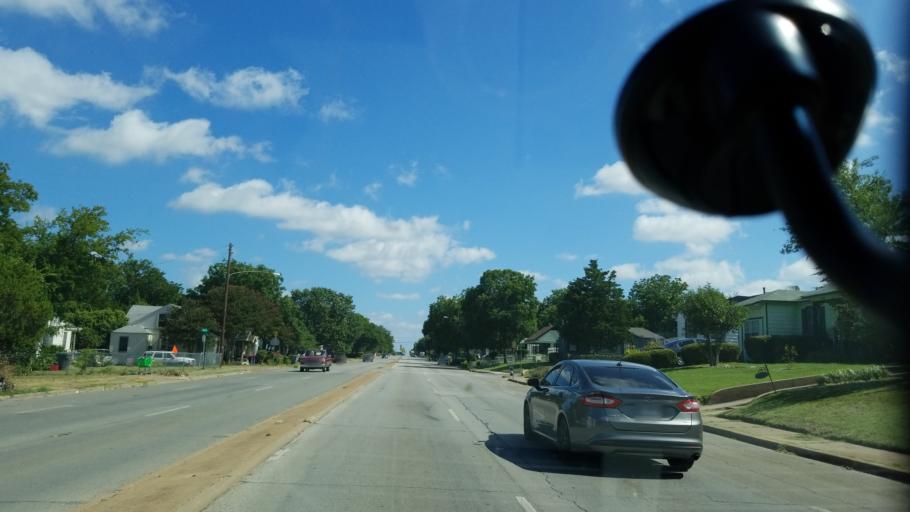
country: US
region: Texas
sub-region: Dallas County
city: Dallas
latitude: 32.7069
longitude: -96.8146
